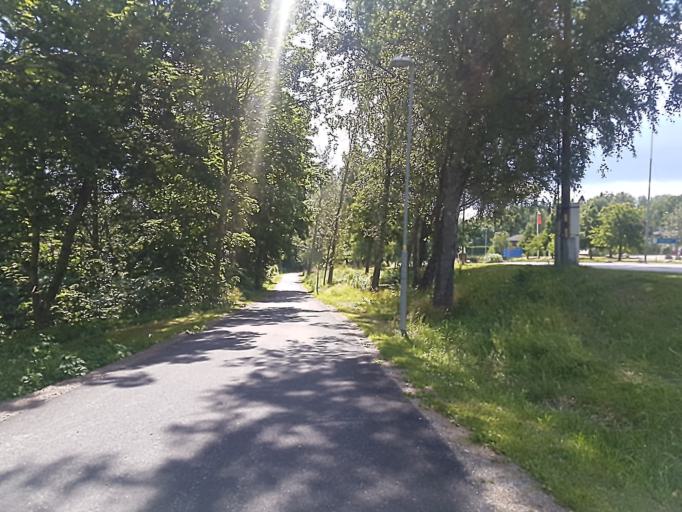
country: SE
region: Soedermanland
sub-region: Gnesta Kommun
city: Gnesta
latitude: 59.0357
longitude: 17.3310
